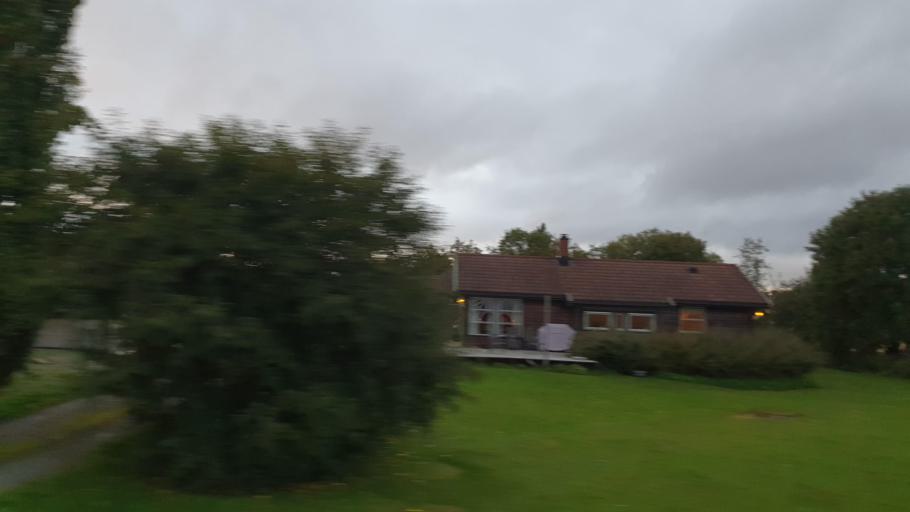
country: NO
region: Nord-Trondelag
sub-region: Levanger
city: Skogn
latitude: 63.6706
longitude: 11.1041
